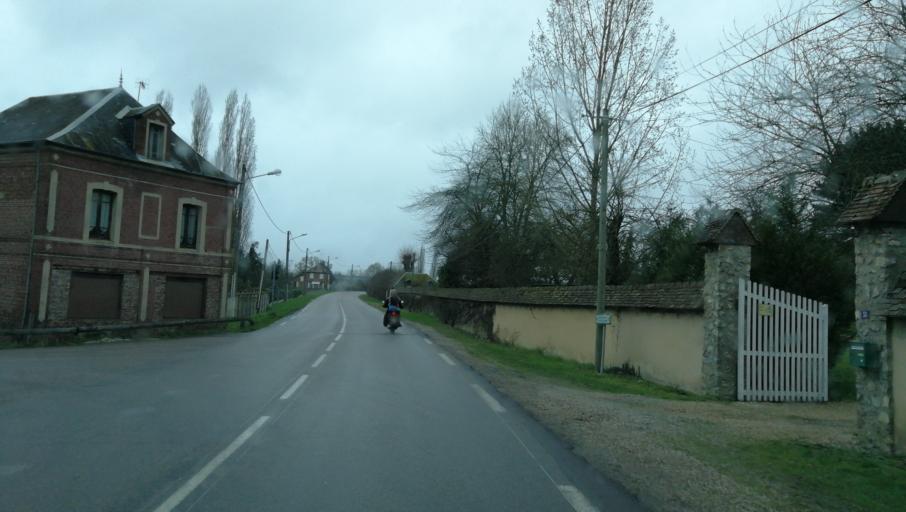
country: FR
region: Haute-Normandie
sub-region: Departement de l'Eure
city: Brionne
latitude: 49.1699
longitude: 0.7236
